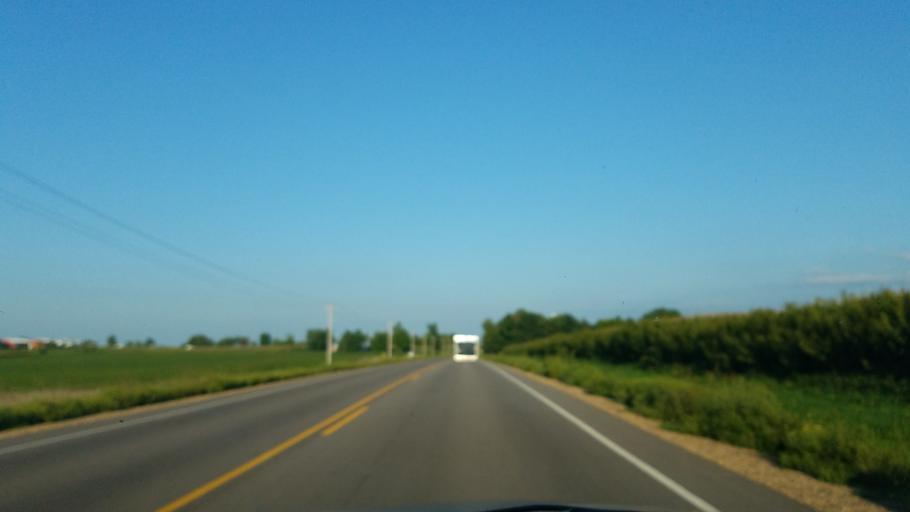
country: US
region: Wisconsin
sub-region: Saint Croix County
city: New Richmond
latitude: 45.0791
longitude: -92.4912
